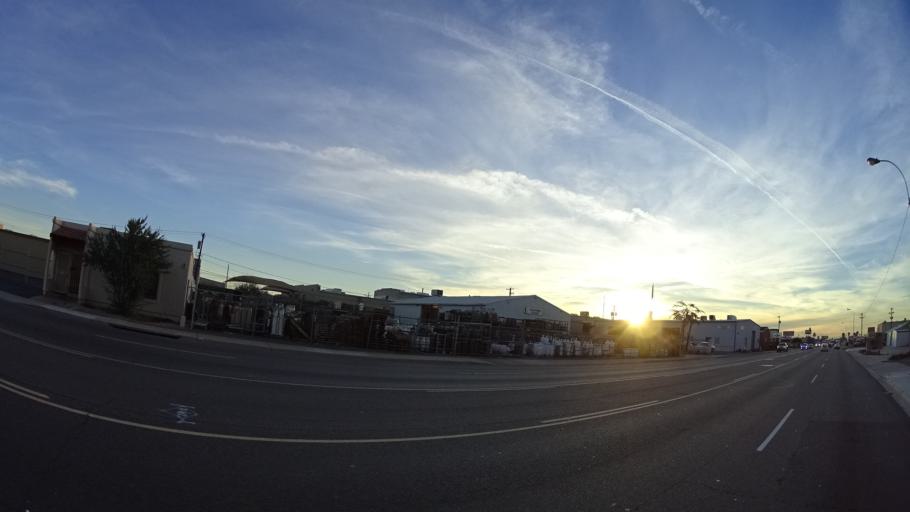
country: US
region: Arizona
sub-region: Maricopa County
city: Tempe Junction
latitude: 33.4220
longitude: -111.9896
